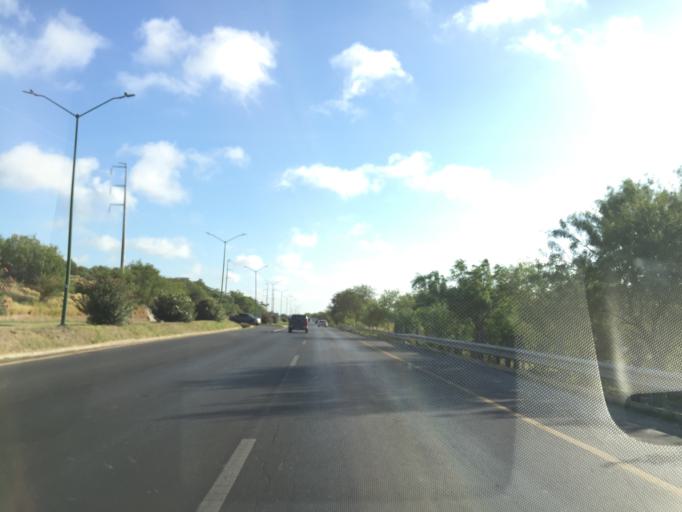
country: MX
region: Tamaulipas
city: Nuevo Laredo
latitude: 27.4595
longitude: -99.4908
